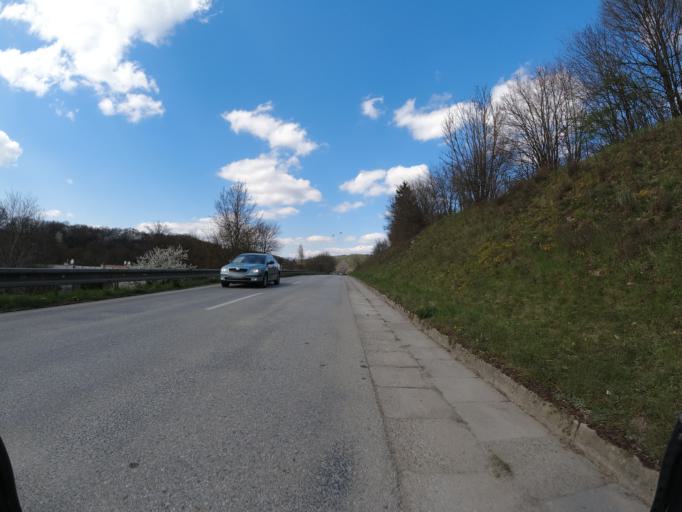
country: SK
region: Nitriansky
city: Stara Tura
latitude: 48.7435
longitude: 17.7220
